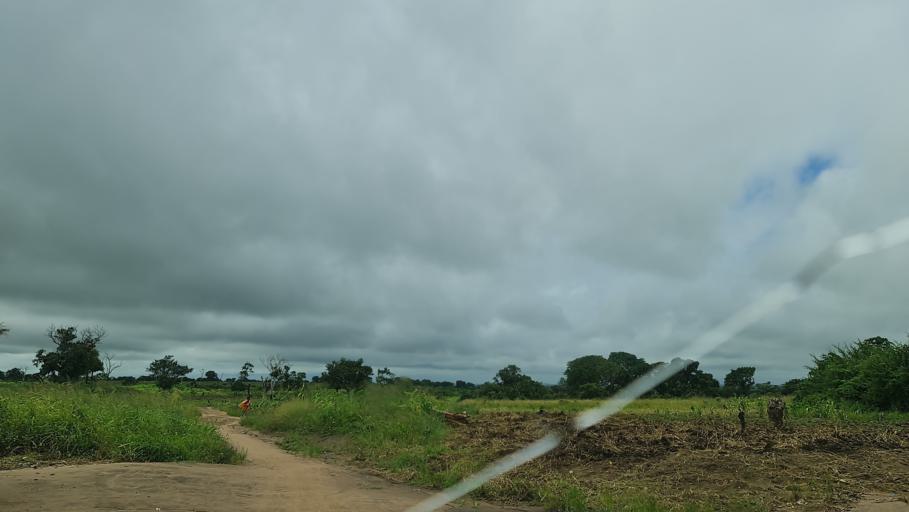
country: MW
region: Southern Region
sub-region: Nsanje District
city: Nsanje
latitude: -17.3382
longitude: 35.7191
